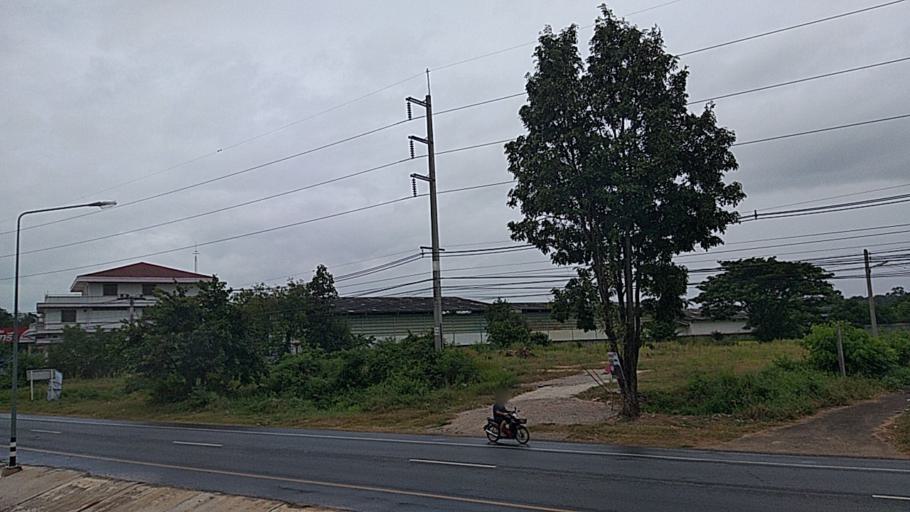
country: TH
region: Maha Sarakham
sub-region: Amphoe Borabue
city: Borabue
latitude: 16.0495
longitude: 103.1276
